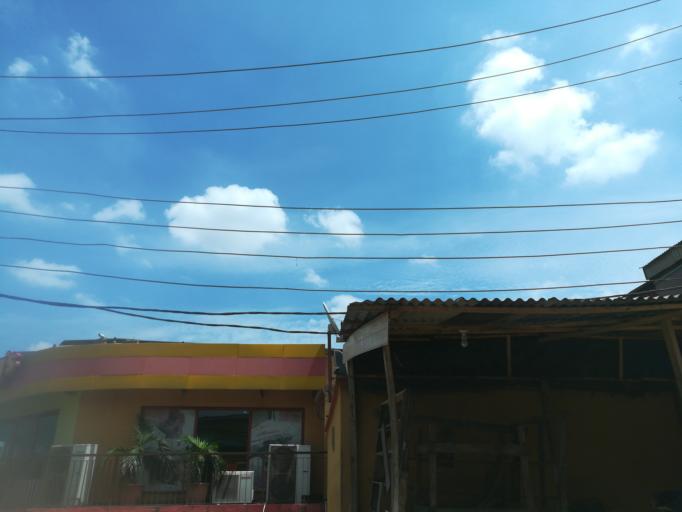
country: NG
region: Lagos
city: Oshodi
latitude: 6.5680
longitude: 3.3323
